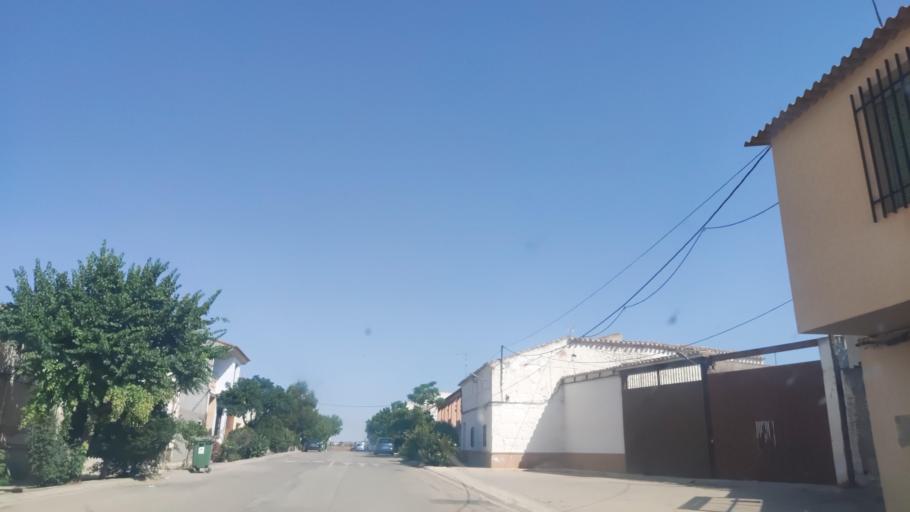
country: ES
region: Castille-La Mancha
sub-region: Provincia de Albacete
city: La Gineta
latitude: 39.1160
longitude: -1.9991
